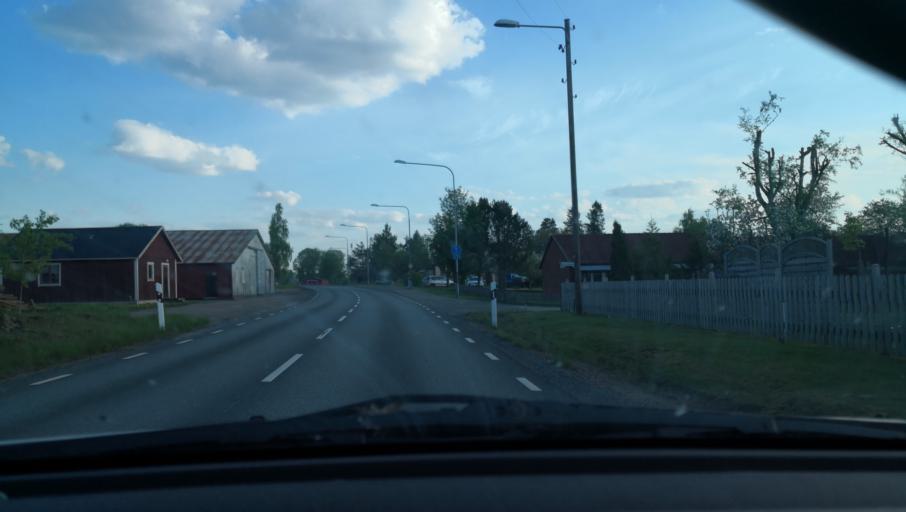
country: SE
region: Joenkoeping
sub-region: Nassjo Kommun
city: Bodafors
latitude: 57.5548
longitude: 14.6991
